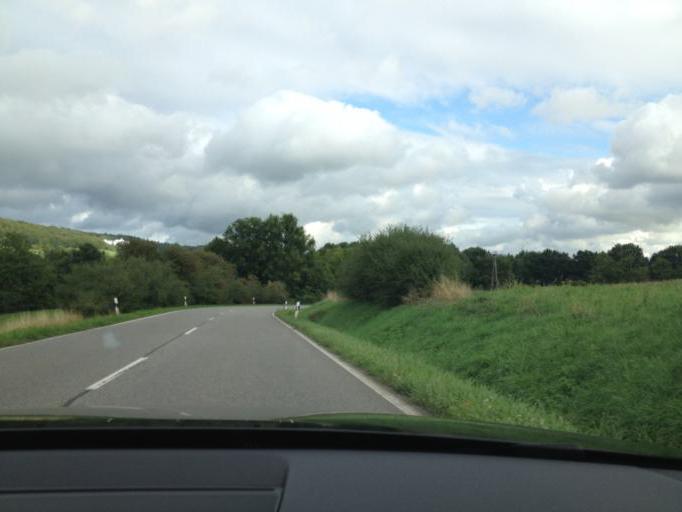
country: DE
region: Saarland
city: Sankt Wendel
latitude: 49.4776
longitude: 7.1700
